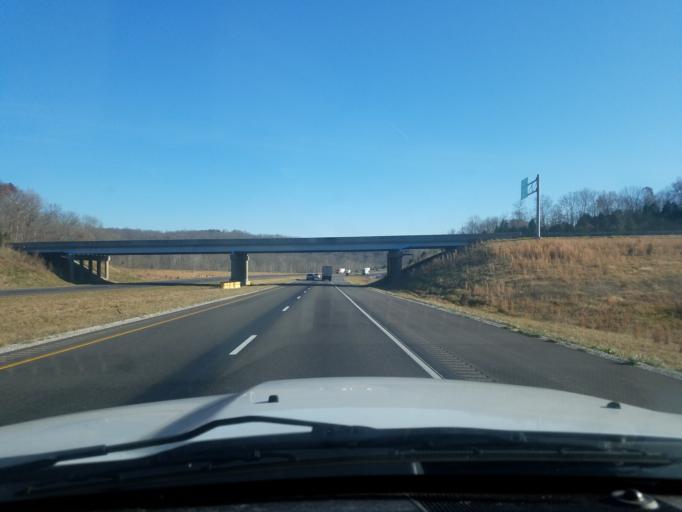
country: US
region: Indiana
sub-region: Crawford County
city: English
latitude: 38.2409
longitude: -86.4691
